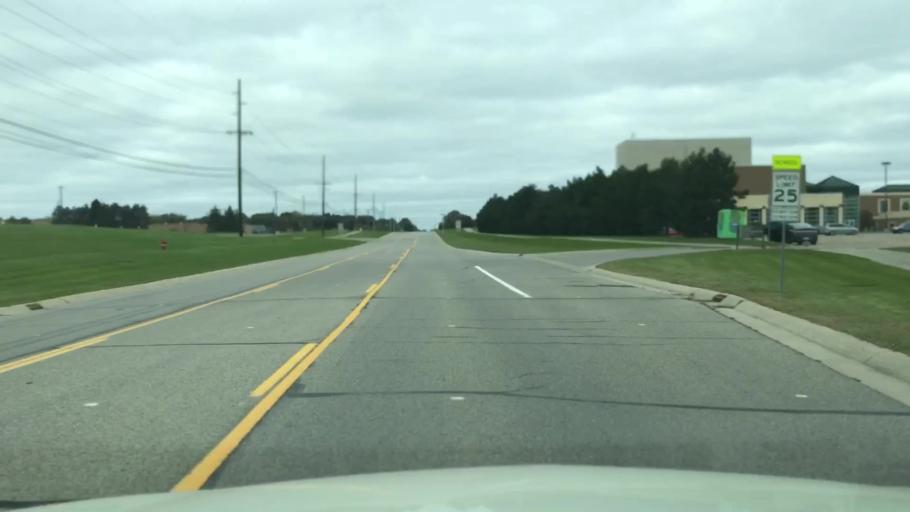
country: US
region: Michigan
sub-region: Oakland County
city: Rochester
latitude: 42.6971
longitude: -83.1234
